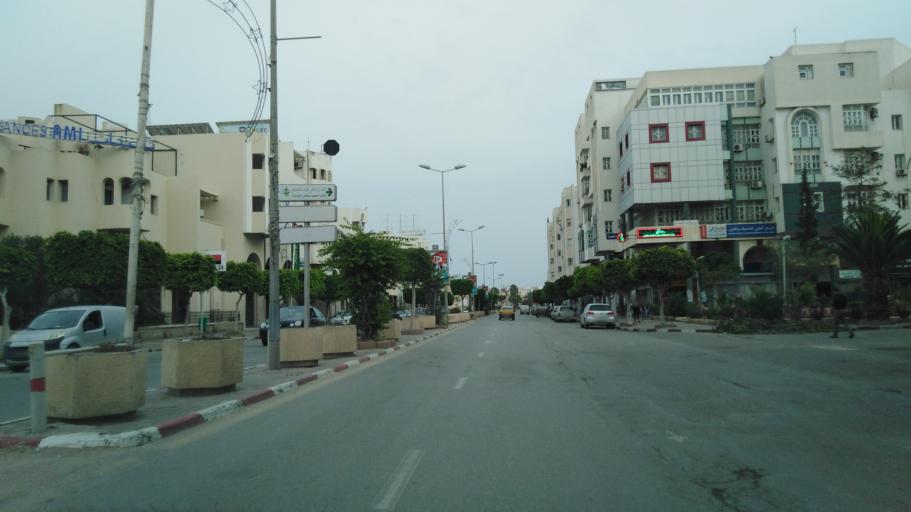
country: TN
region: Safaqis
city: Sfax
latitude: 34.7384
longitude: 10.7547
